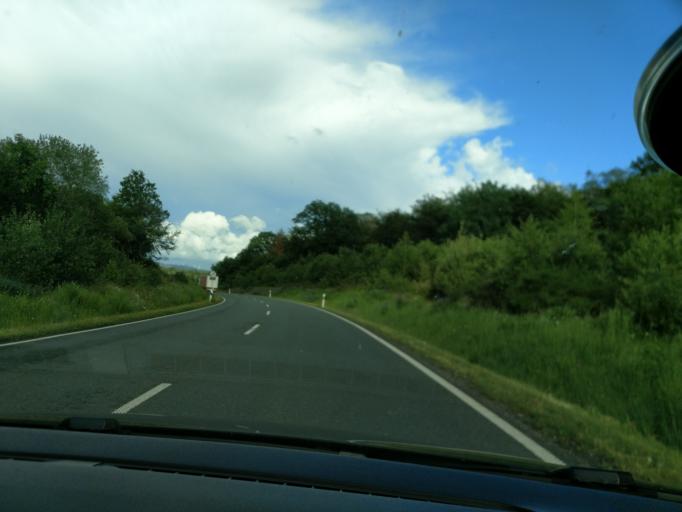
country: DE
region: Hesse
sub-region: Regierungsbezirk Kassel
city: Bad Arolsen
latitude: 51.3579
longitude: 8.9904
